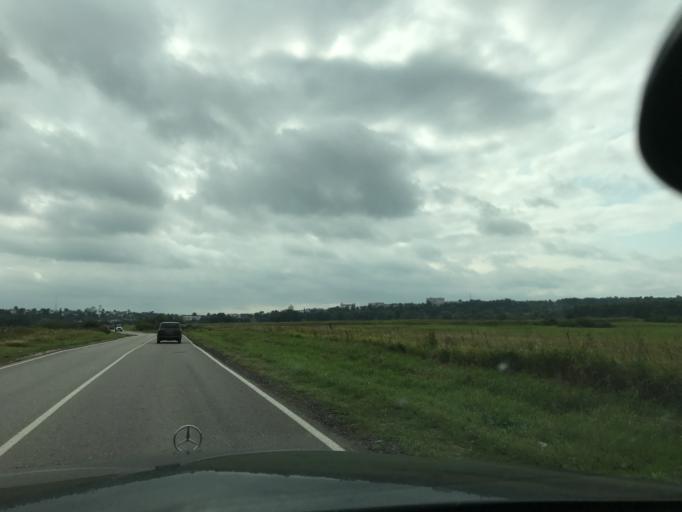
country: RU
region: Nizjnij Novgorod
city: Pavlovo
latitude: 55.9777
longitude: 43.0515
